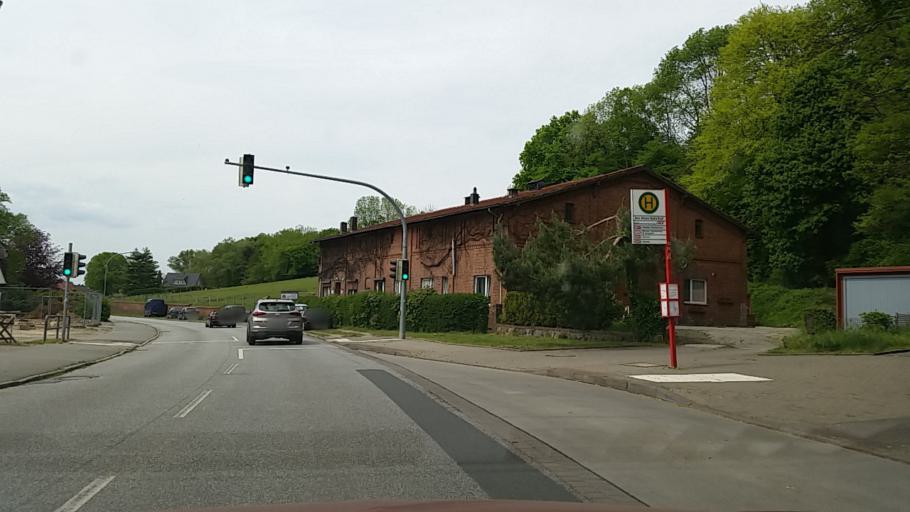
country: DE
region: Schleswig-Holstein
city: Escheburg
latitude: 53.4632
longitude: 10.3128
